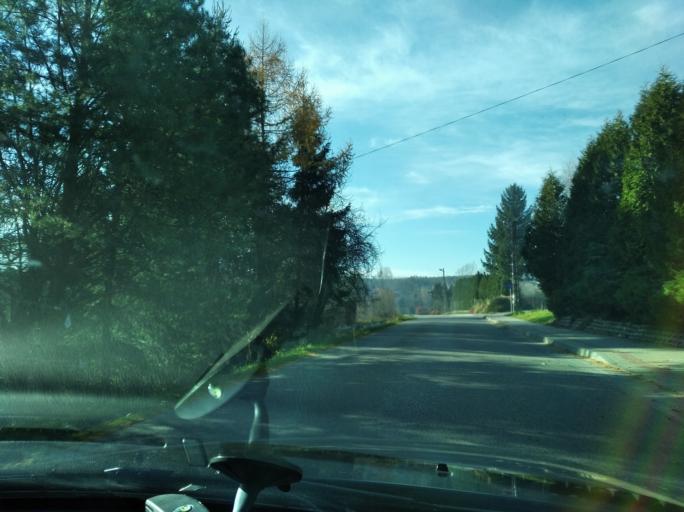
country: PL
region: Subcarpathian Voivodeship
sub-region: Powiat rzeszowski
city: Lutoryz
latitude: 49.9672
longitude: 21.9057
